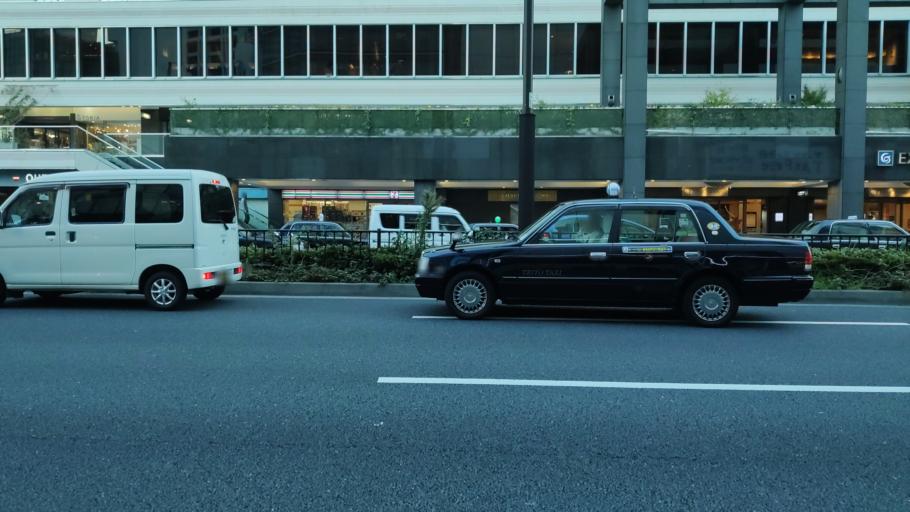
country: JP
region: Tokyo
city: Tokyo
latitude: 35.6773
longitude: 139.7372
